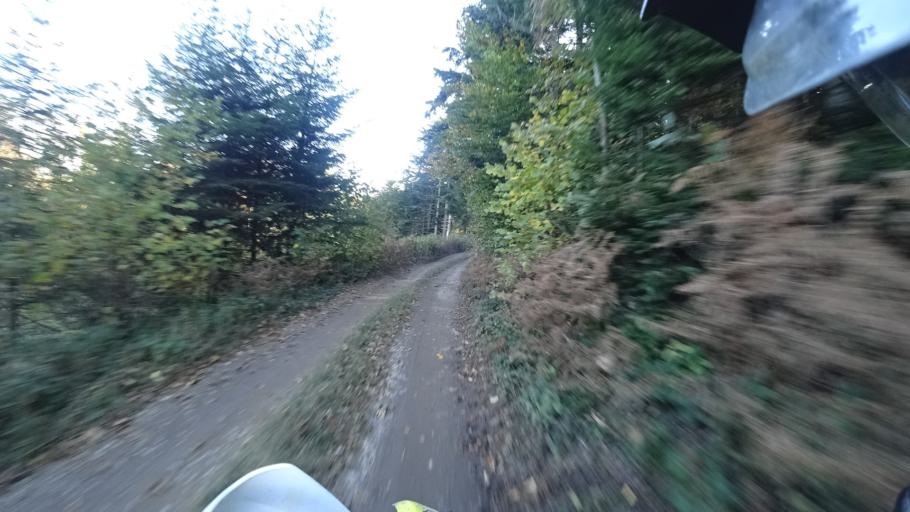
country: HR
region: Karlovacka
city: Plaski
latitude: 45.0210
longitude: 15.3925
